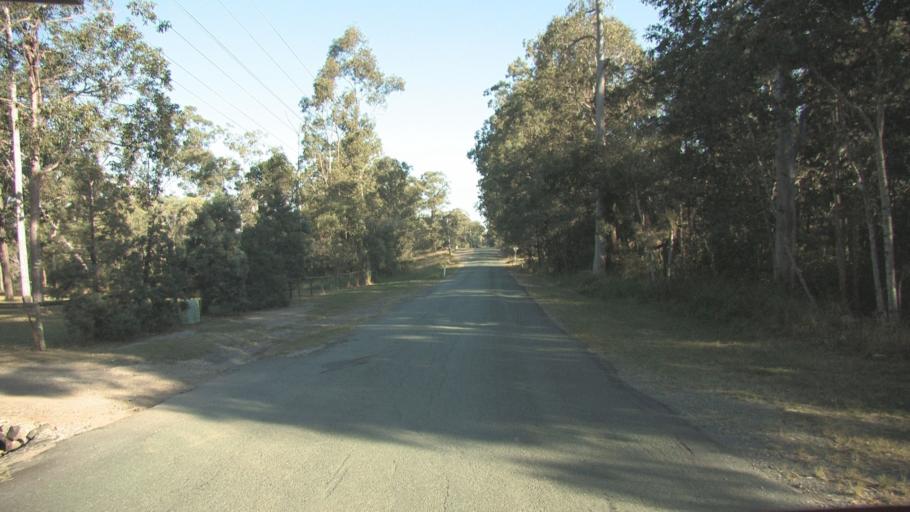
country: AU
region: Queensland
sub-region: Ipswich
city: Springfield Lakes
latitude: -27.7056
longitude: 152.9475
